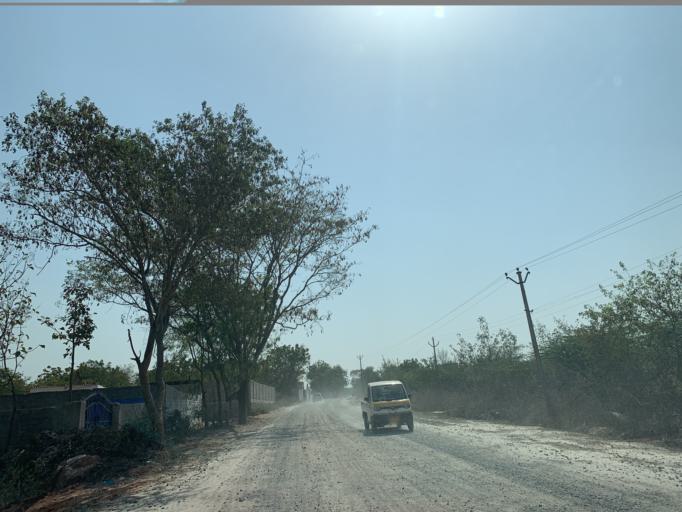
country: IN
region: Telangana
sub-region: Rangareddi
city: Sriramnagar
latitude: 17.3286
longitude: 78.2958
